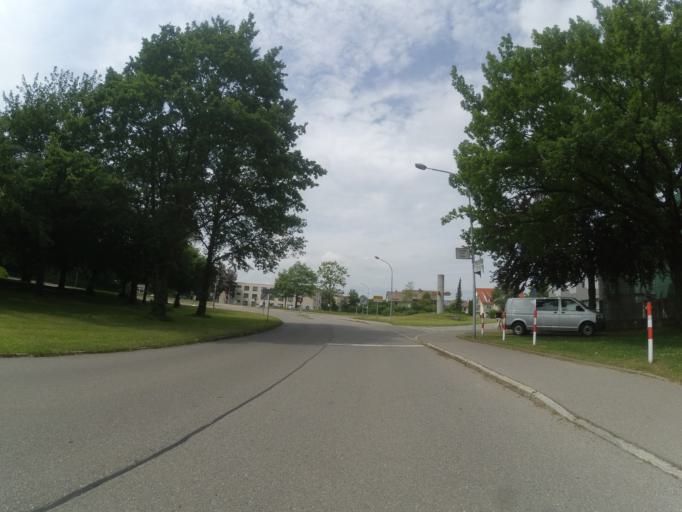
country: DE
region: Baden-Wuerttemberg
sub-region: Tuebingen Region
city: Leutkirch im Allgau
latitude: 47.8193
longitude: 10.0199
